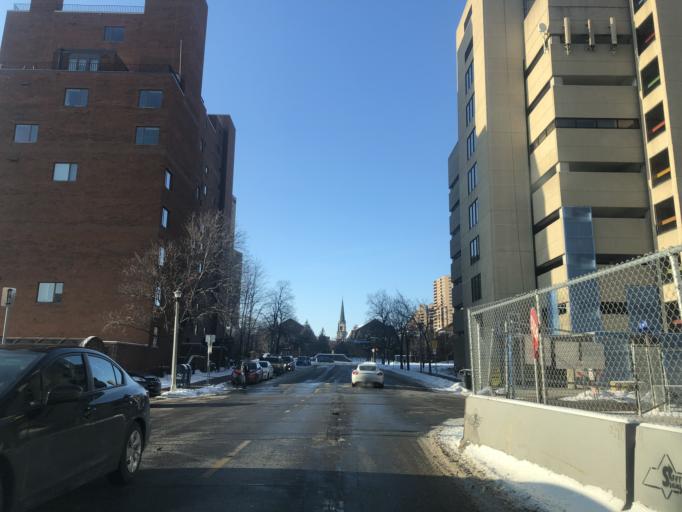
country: US
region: Minnesota
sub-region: Hennepin County
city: Minneapolis
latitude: 44.9852
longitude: -93.2541
